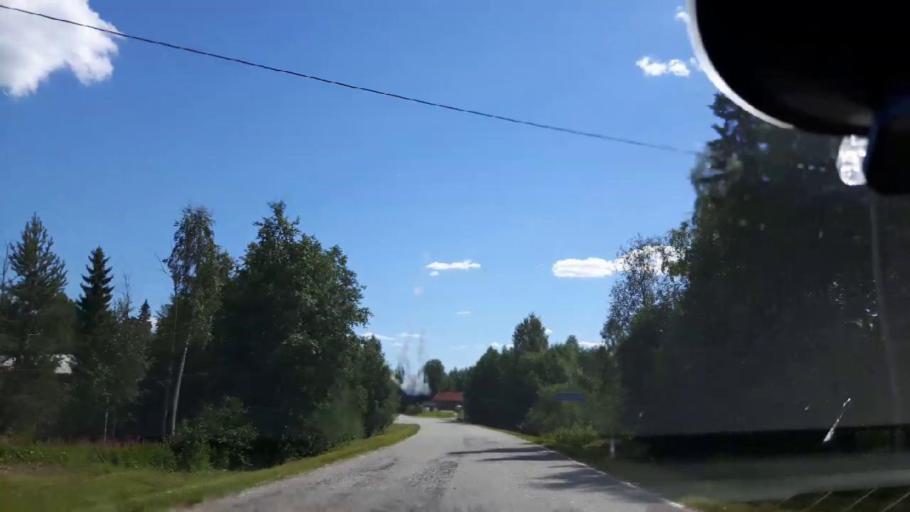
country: SE
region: Vaesternorrland
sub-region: Ange Kommun
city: Fransta
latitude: 62.7979
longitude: 16.2074
